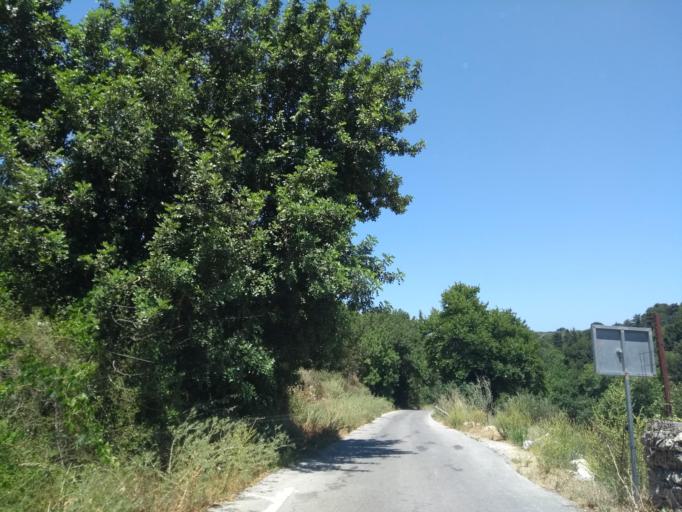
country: GR
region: Crete
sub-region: Nomos Chanias
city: Georgioupolis
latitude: 35.3172
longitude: 24.3058
